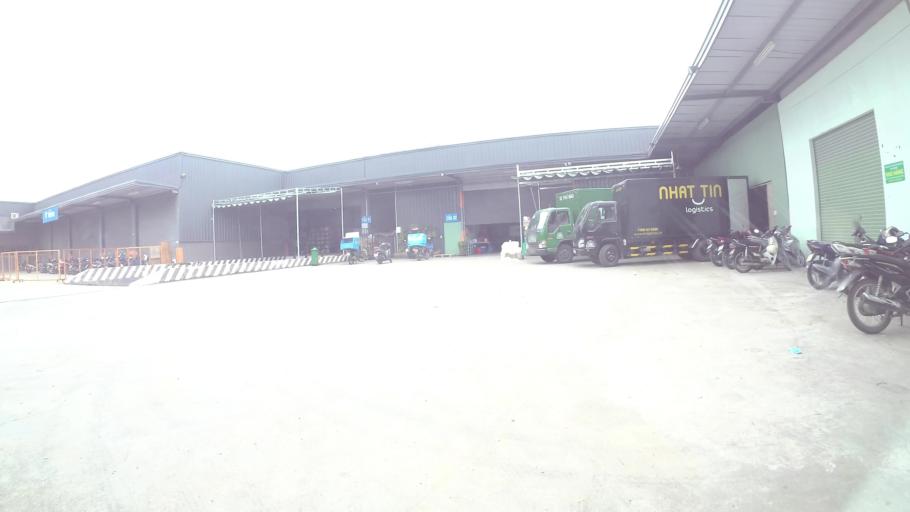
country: VN
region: Da Nang
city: Da Nang
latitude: 16.0517
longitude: 108.2072
